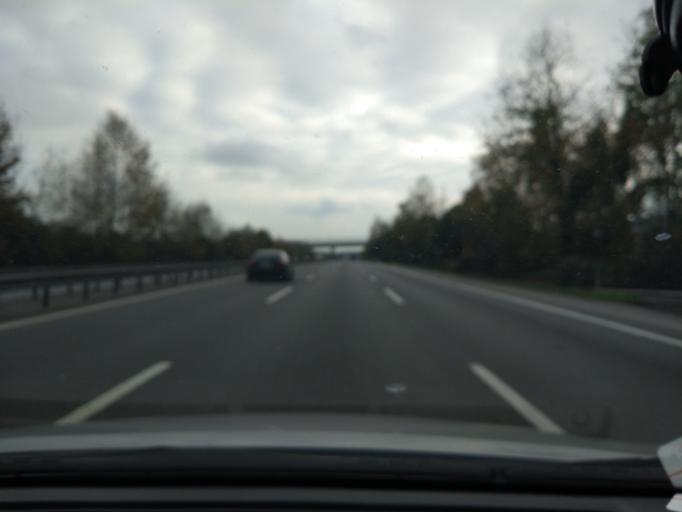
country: TR
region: Kocaeli
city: Derbent
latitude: 40.7105
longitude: 30.1333
